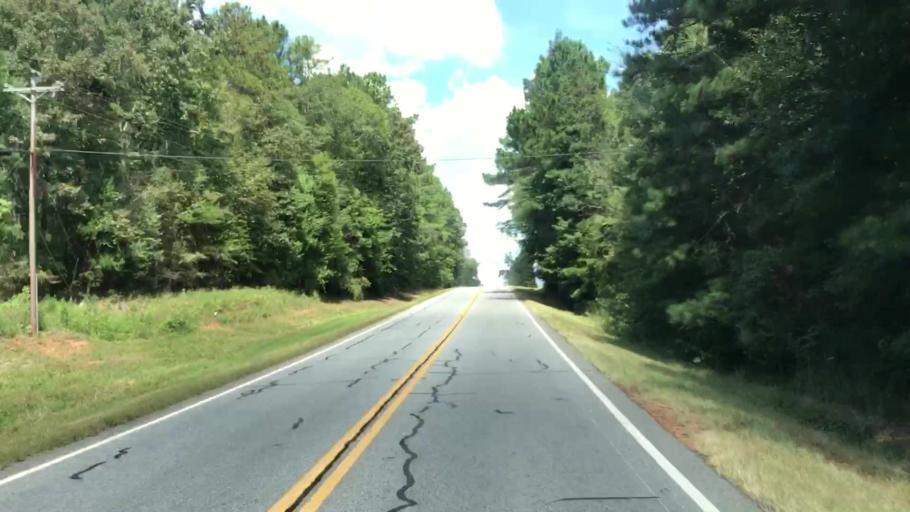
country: US
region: Georgia
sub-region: Oconee County
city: Watkinsville
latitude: 33.7680
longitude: -83.3098
